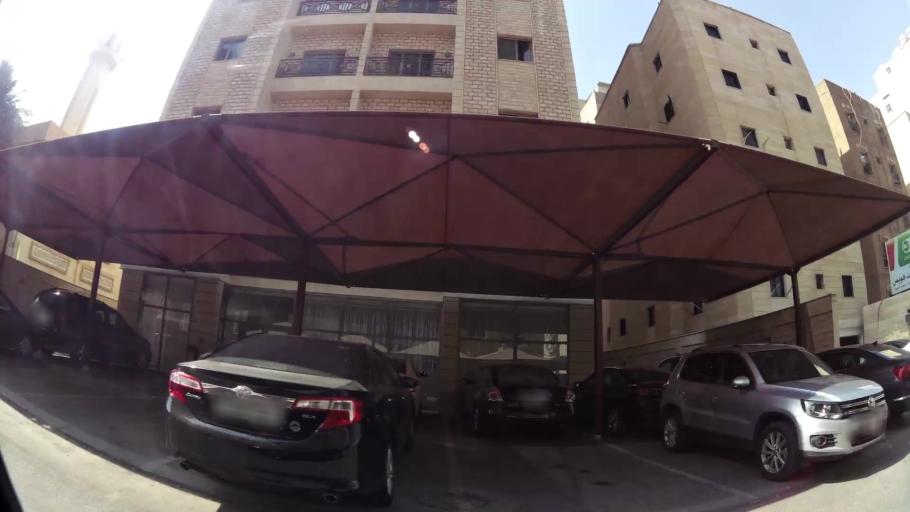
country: KW
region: Muhafazat Hawalli
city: Hawalli
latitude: 29.3356
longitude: 48.0329
